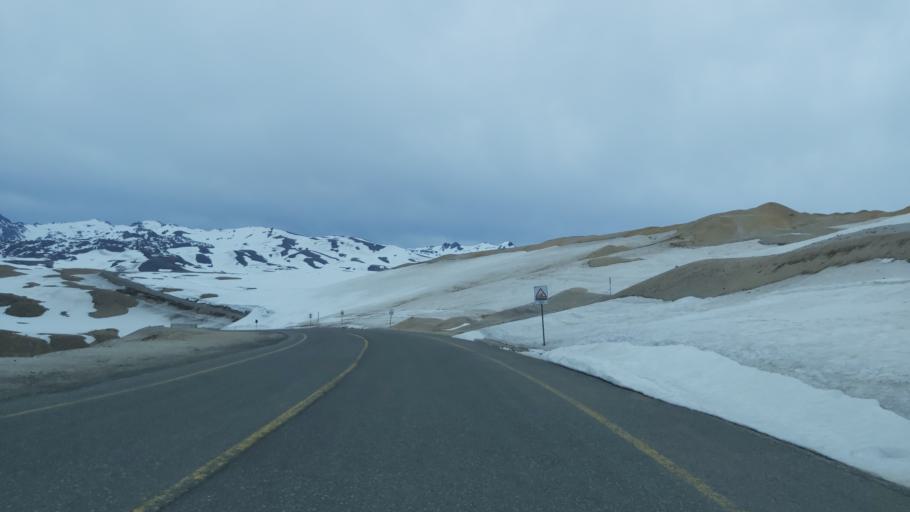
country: CL
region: Maule
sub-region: Provincia de Linares
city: Colbun
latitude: -36.0185
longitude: -70.5211
